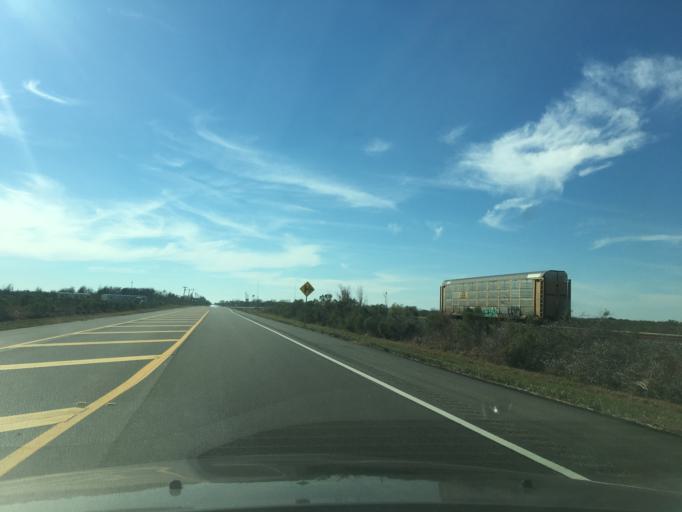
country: US
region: Texas
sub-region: Wharton County
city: East Bernard
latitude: 29.4584
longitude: -95.9823
